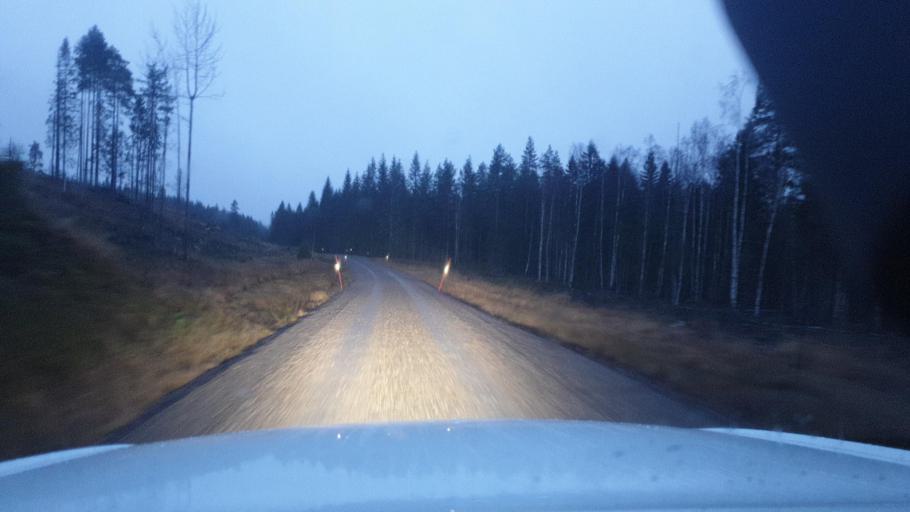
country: SE
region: Vaermland
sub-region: Eda Kommun
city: Charlottenberg
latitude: 60.0753
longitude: 12.6207
